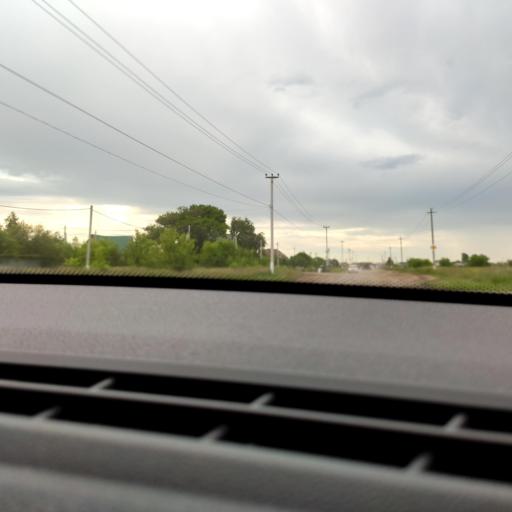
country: RU
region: Samara
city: Podstepki
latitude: 53.5190
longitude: 49.1341
